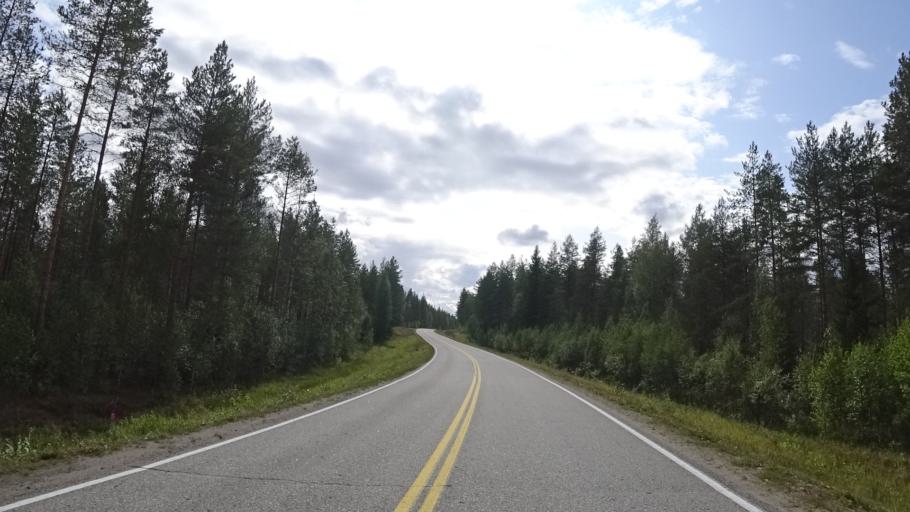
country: FI
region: North Karelia
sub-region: Joensuu
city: Ilomantsi
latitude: 62.7918
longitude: 31.0999
